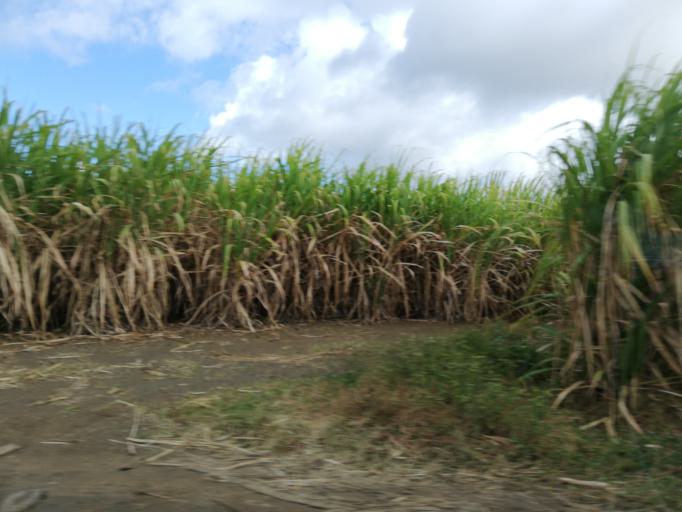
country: MU
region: Flacq
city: Grande Riviere Sud Est
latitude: -20.2754
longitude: 57.7641
